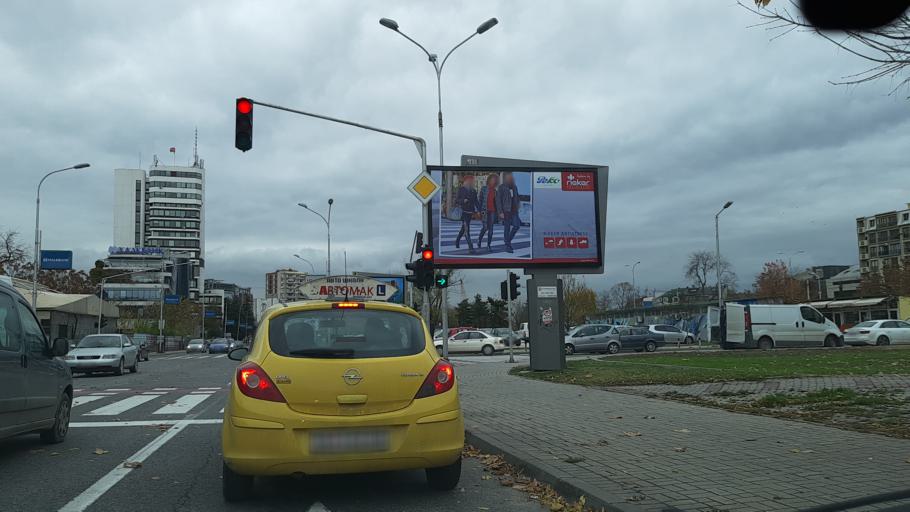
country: MK
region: Karpos
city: Skopje
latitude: 41.9939
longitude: 21.4210
